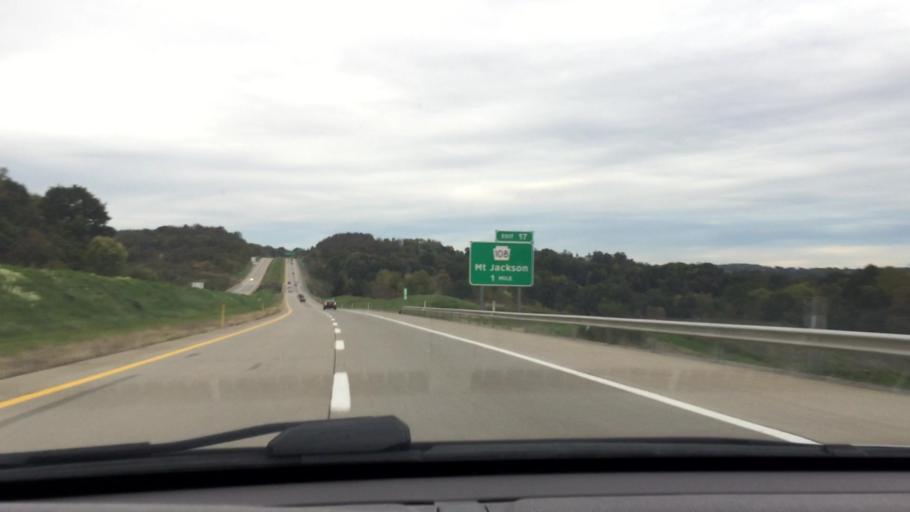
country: US
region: Pennsylvania
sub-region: Lawrence County
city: Oakland
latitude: 40.9527
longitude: -80.3929
